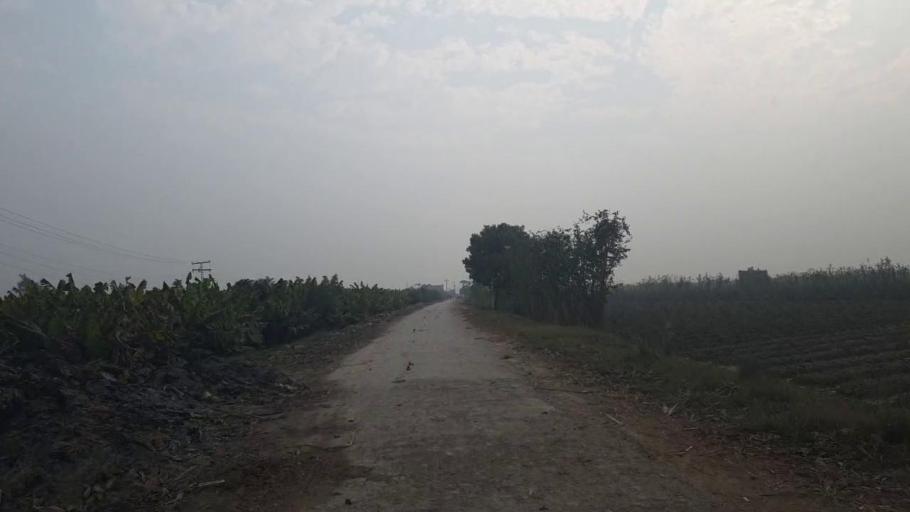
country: PK
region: Sindh
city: Berani
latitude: 25.8027
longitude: 68.7325
